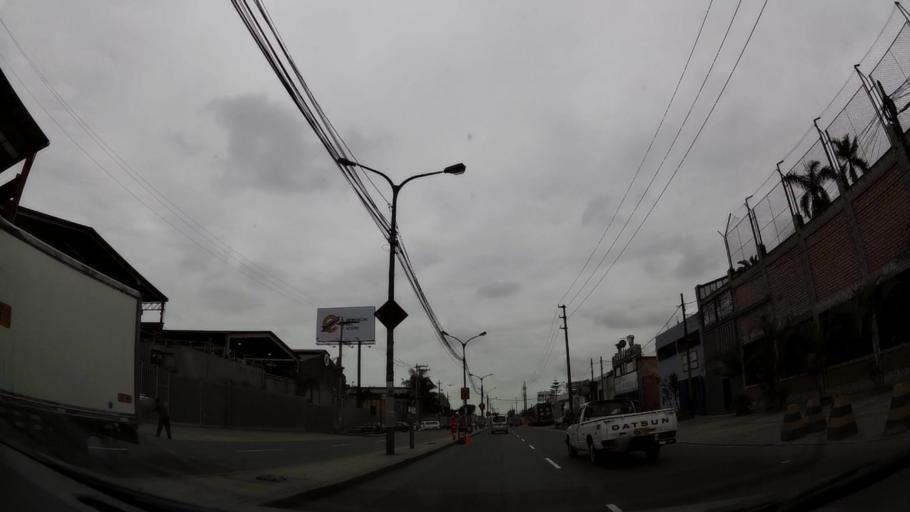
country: PE
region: Lima
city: Lima
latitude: -12.0457
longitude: -77.0675
